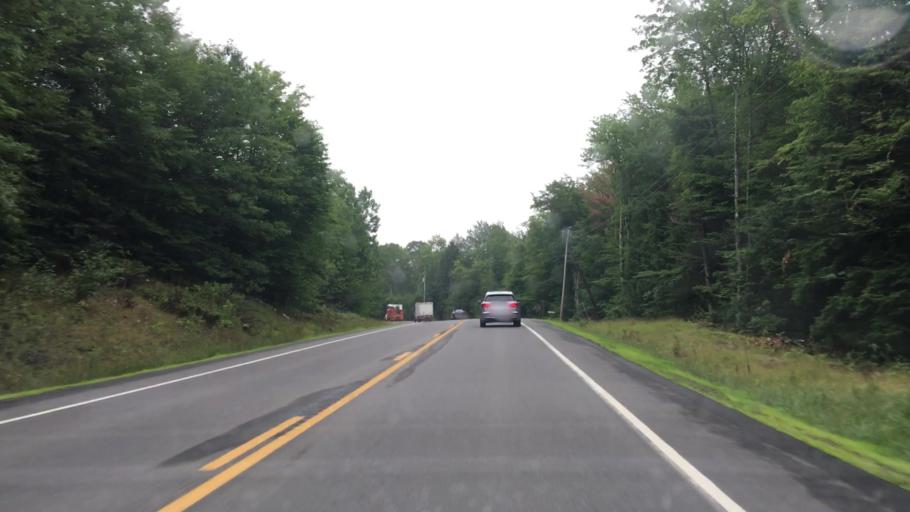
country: US
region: Maine
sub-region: Knox County
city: Washington
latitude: 44.2469
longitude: -69.3983
